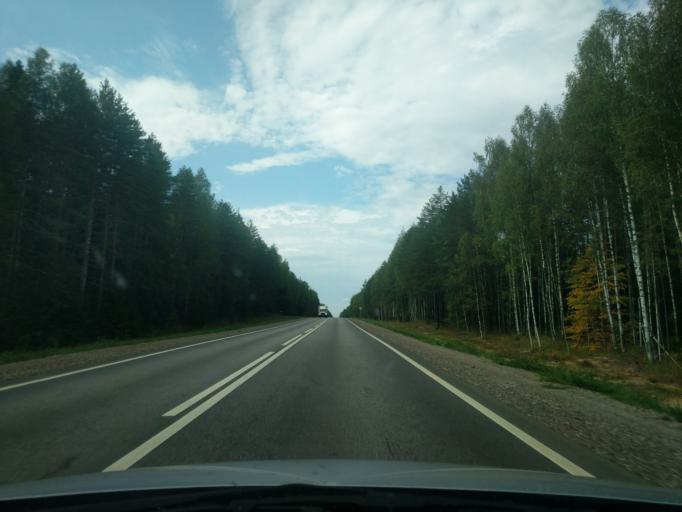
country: RU
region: Kostroma
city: Kadyy
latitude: 57.7952
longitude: 42.9439
